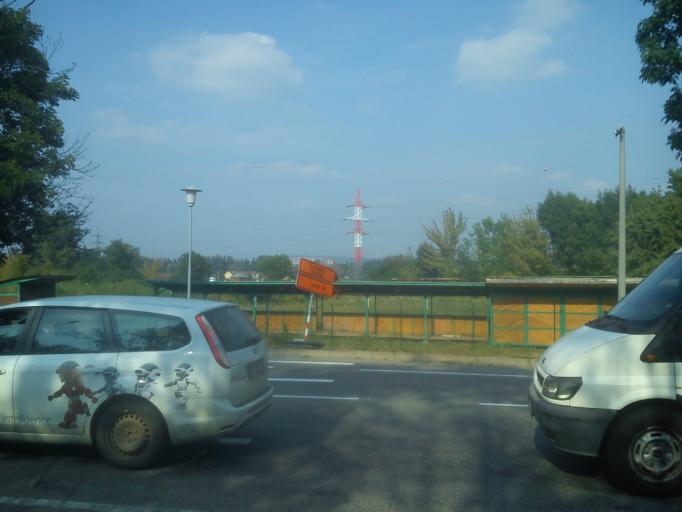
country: CZ
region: South Moravian
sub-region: Mesto Brno
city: Brno
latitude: 49.1634
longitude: 16.6334
